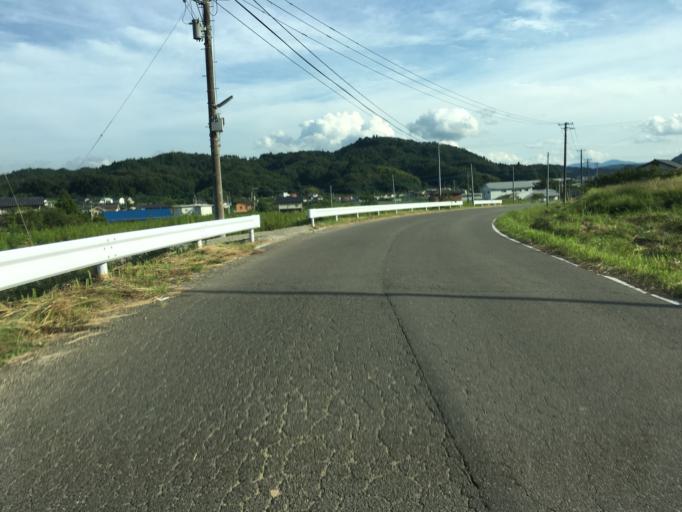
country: JP
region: Fukushima
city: Hobaramachi
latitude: 37.7949
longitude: 140.5942
